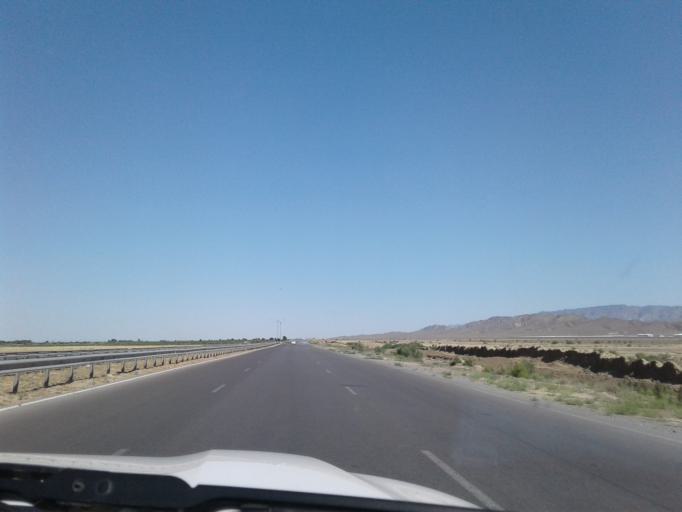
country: TM
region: Ahal
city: Annau
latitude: 37.8034
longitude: 58.7955
